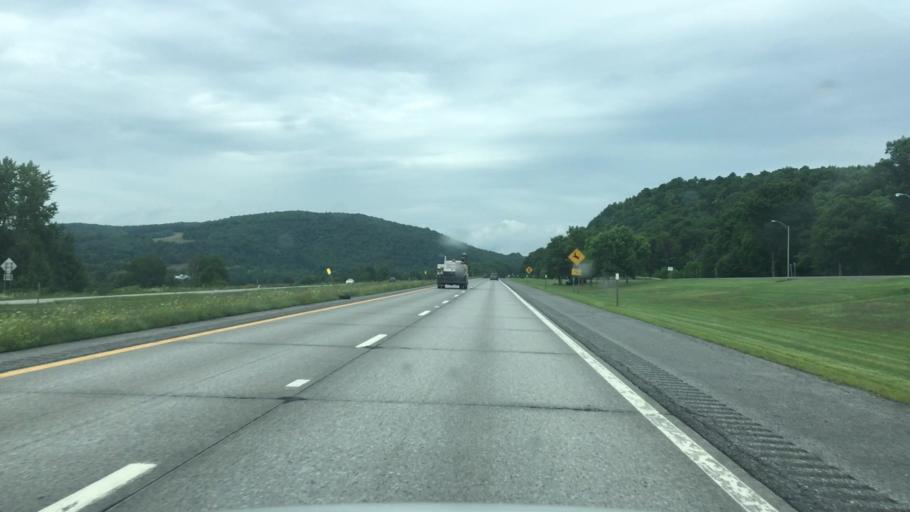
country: US
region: New York
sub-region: Otsego County
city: Worcester
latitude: 42.5725
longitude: -74.7676
